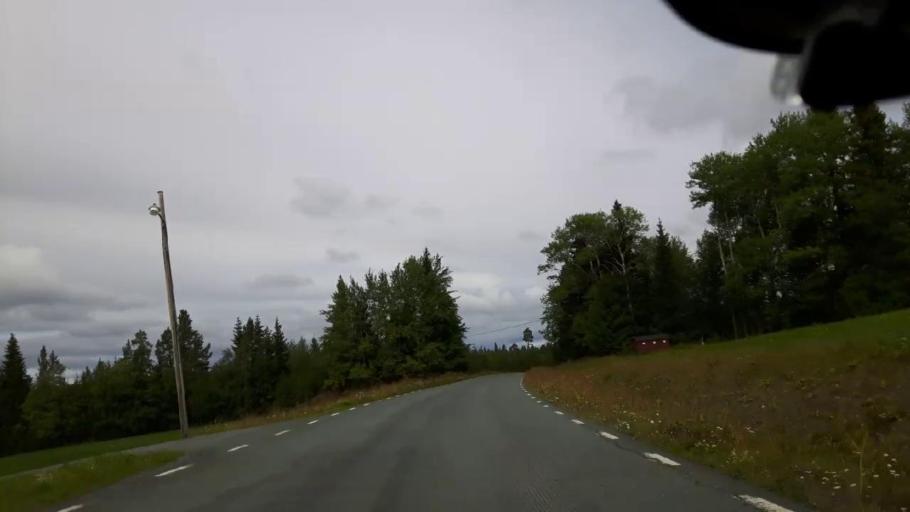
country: SE
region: Jaemtland
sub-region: Krokoms Kommun
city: Valla
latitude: 63.4554
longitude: 14.0437
